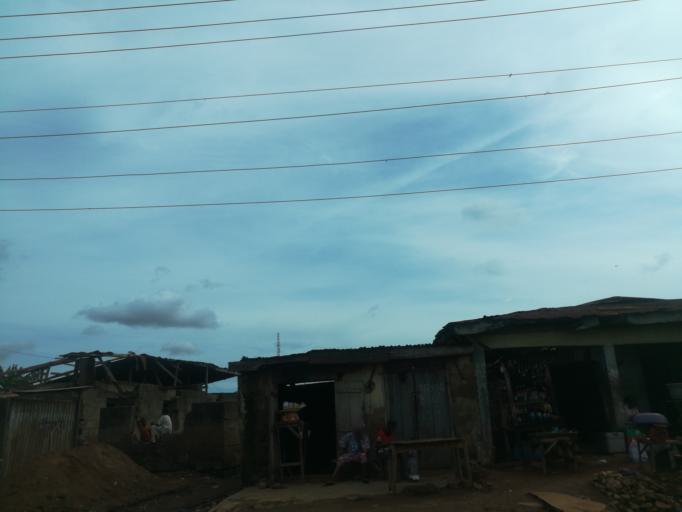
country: NG
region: Oyo
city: Ibadan
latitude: 7.3774
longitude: 3.9560
